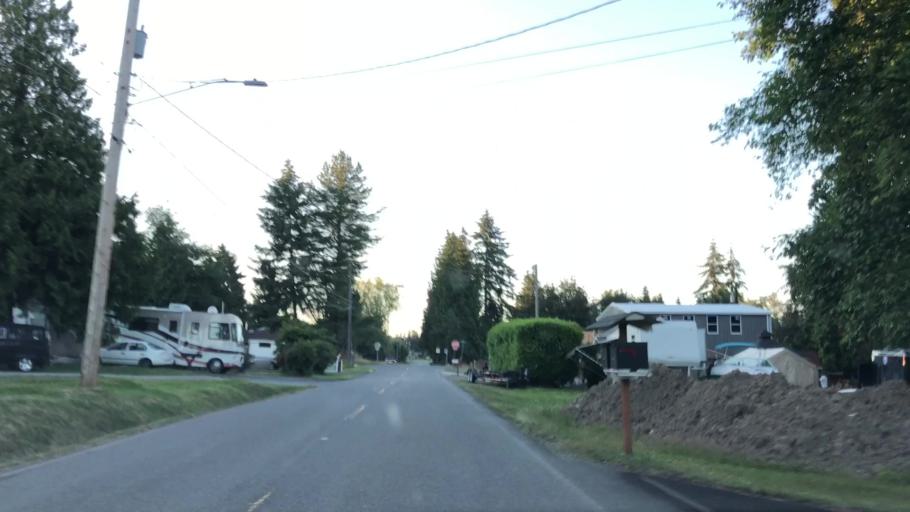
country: US
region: Washington
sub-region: Snohomish County
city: Brier
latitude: 47.7873
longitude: -122.2720
